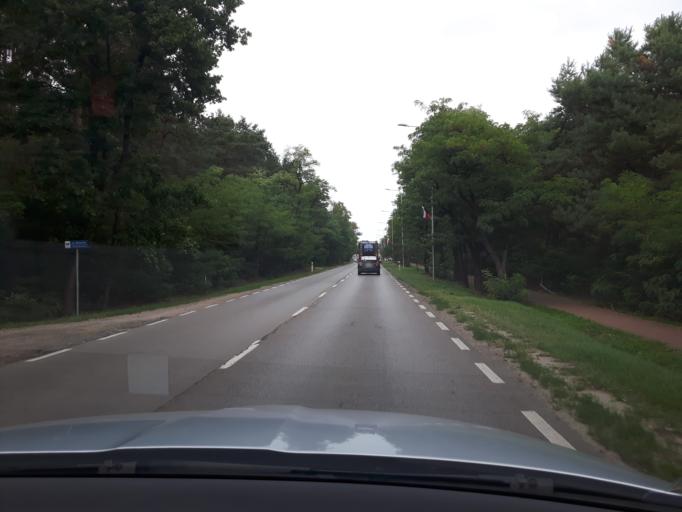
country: PL
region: Masovian Voivodeship
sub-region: Powiat legionowski
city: Stanislawow Pierwszy
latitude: 52.3999
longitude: 21.0364
